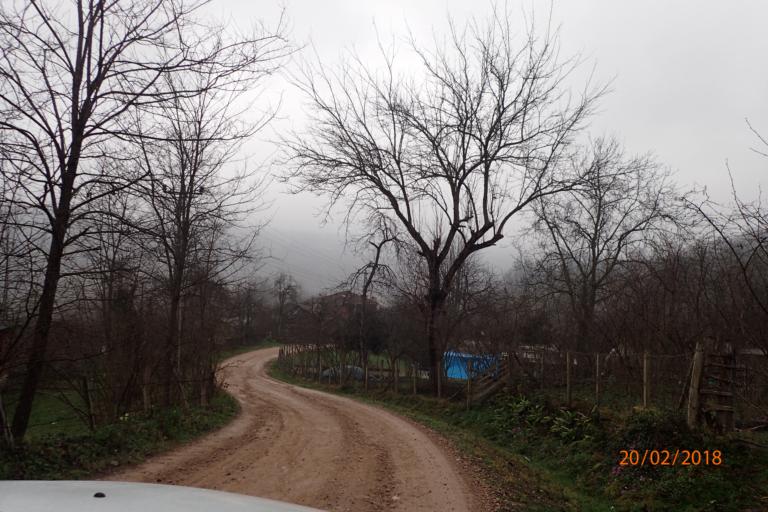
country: TR
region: Ordu
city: Camas
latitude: 40.9475
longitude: 37.5243
